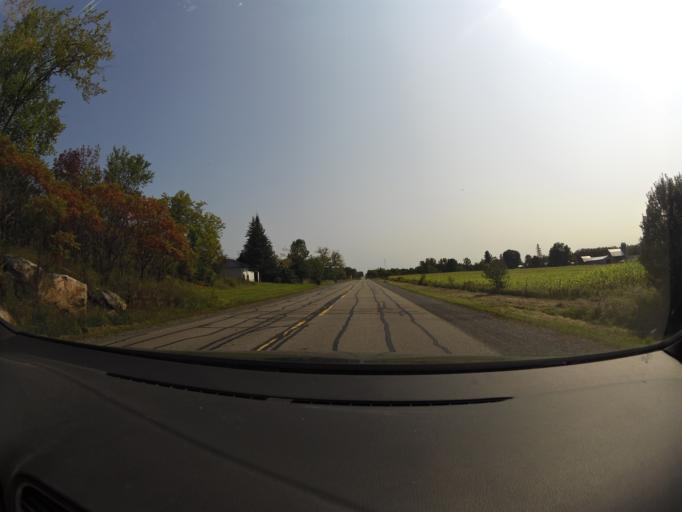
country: CA
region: Ontario
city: Arnprior
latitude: 45.4308
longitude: -76.1682
